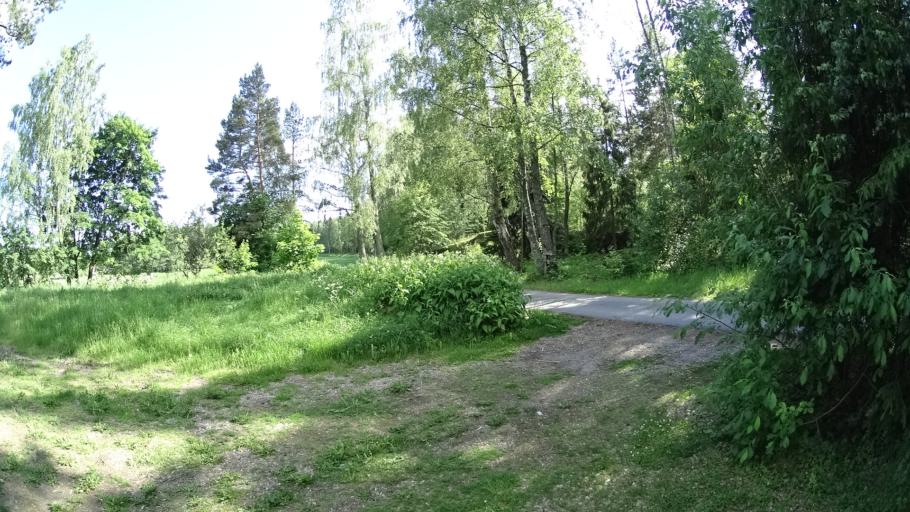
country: FI
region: Uusimaa
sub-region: Helsinki
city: Vantaa
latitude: 60.2386
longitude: 25.1823
